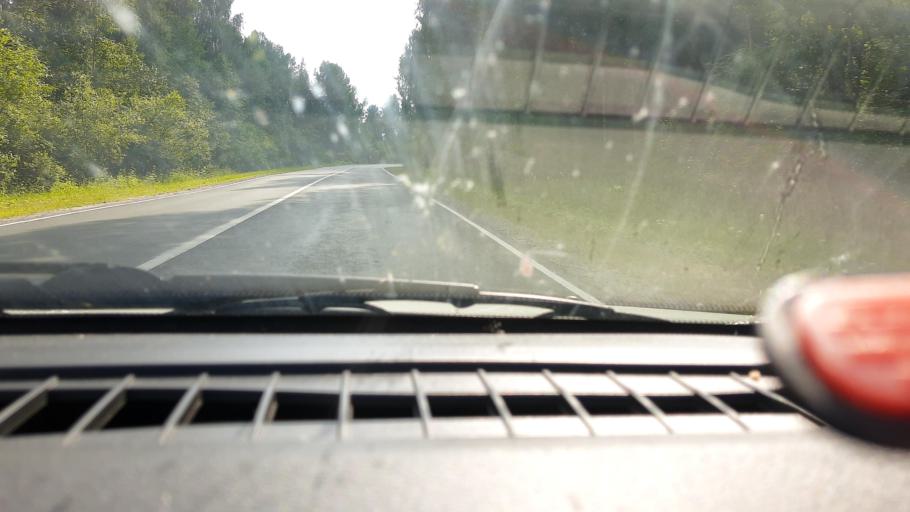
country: RU
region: Nizjnij Novgorod
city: Uren'
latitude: 57.2498
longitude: 45.6030
